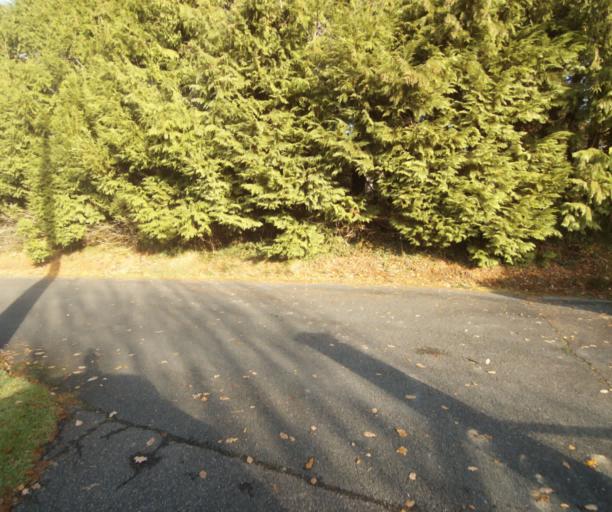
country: FR
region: Limousin
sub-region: Departement de la Correze
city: Laguenne
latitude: 45.2538
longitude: 1.7967
